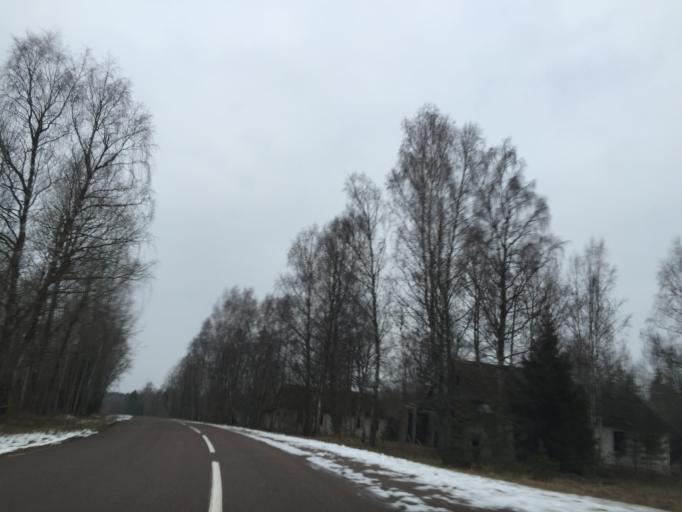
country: EE
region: Saare
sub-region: Kuressaare linn
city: Kuressaare
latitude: 58.3927
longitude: 22.2072
